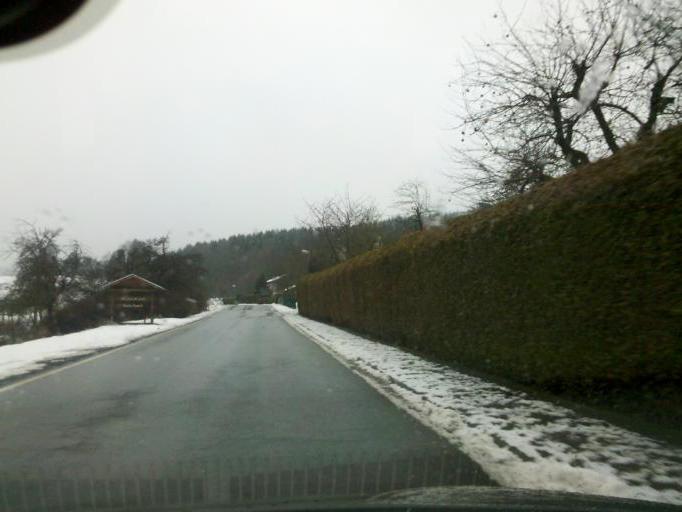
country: DE
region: Hesse
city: Dillenburg
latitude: 50.8292
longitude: 8.3041
